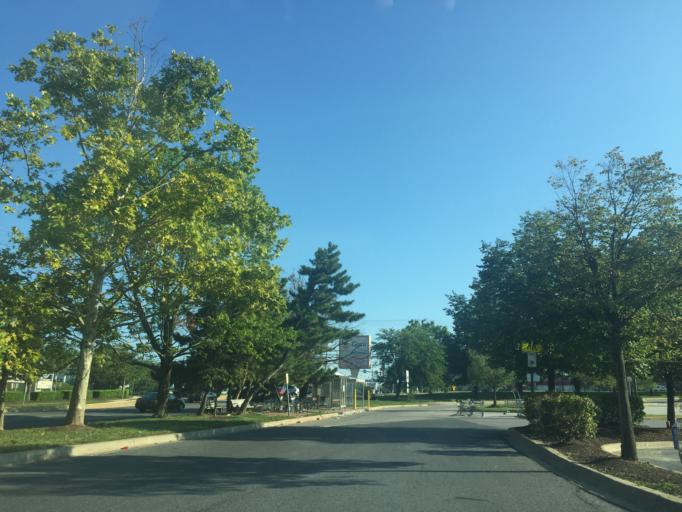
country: US
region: Maryland
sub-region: Baltimore County
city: Catonsville
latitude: 39.2823
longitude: -76.7535
